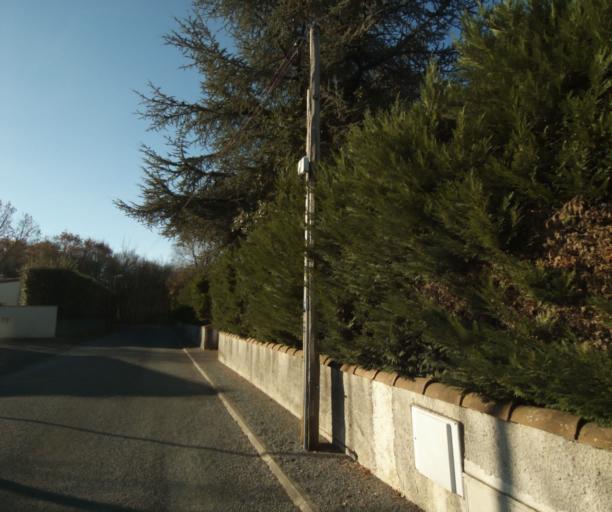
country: FR
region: Poitou-Charentes
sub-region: Departement de la Charente-Maritime
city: Fontcouverte
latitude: 45.7658
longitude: -0.5856
